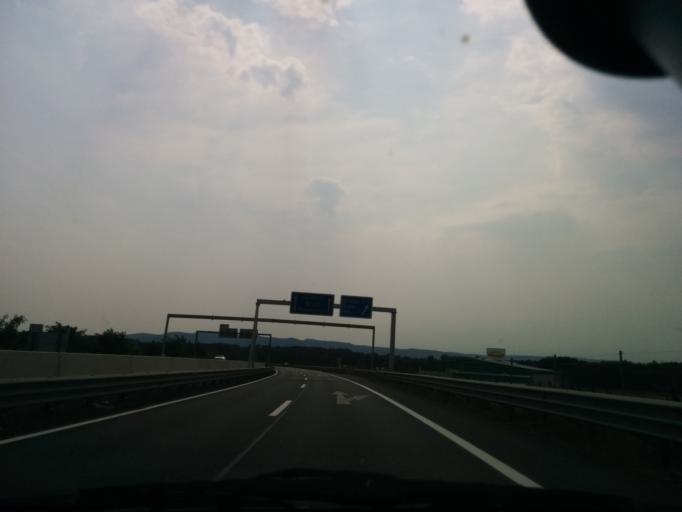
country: AT
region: Lower Austria
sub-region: Politischer Bezirk Korneuburg
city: Stockerau
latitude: 48.3857
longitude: 16.1795
